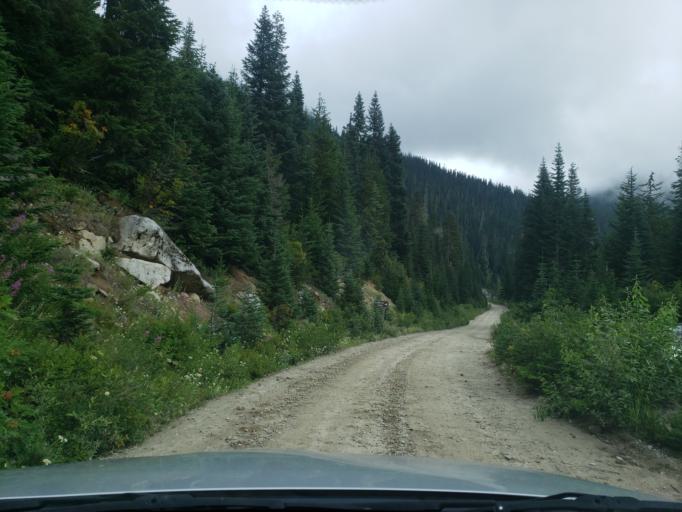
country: US
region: Washington
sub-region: Chelan County
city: Leavenworth
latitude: 47.8025
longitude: -121.0771
